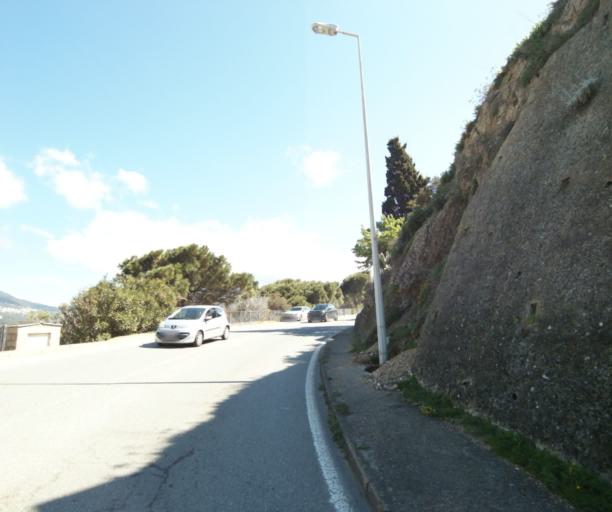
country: FR
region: Corsica
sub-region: Departement de la Corse-du-Sud
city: Propriano
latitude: 41.6792
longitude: 8.9112
